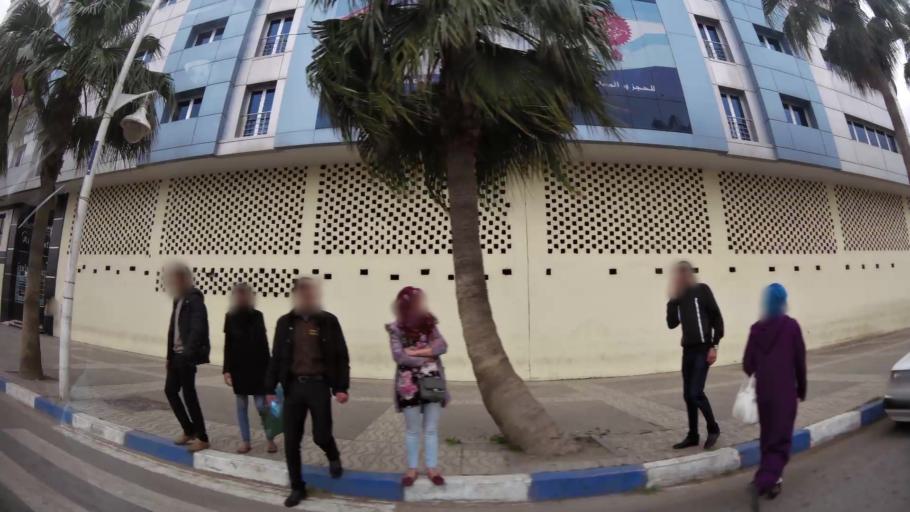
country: MA
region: Oriental
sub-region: Nador
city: Nador
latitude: 35.1530
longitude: -2.9289
